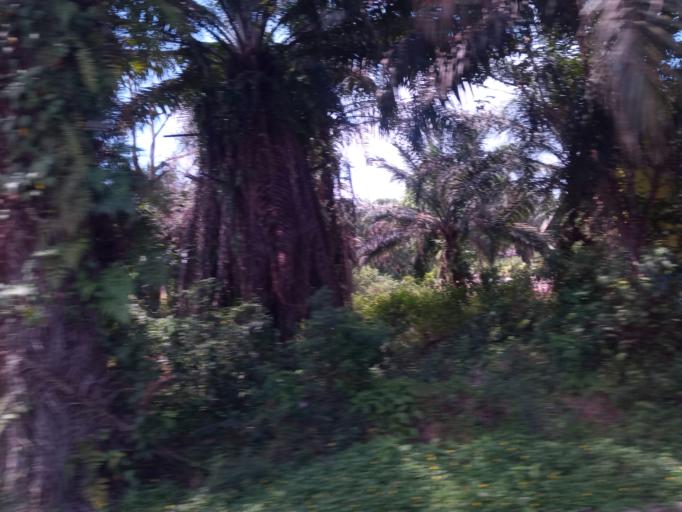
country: ID
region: Jambi
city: Muara Tembesi
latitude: -1.6787
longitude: 103.0914
